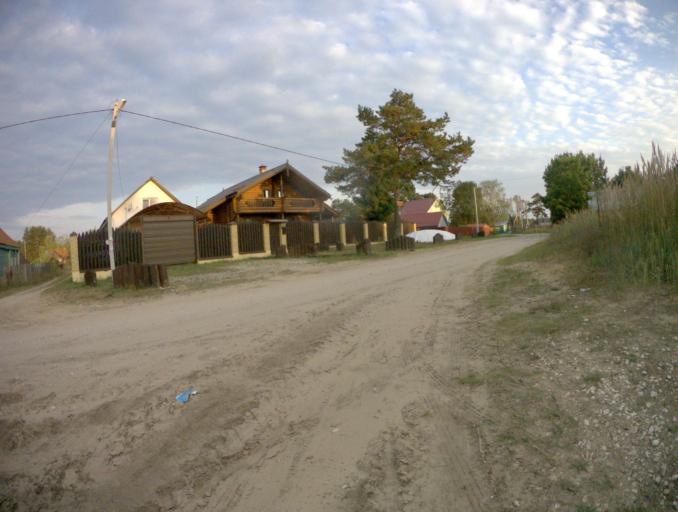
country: RU
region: Vladimir
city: Raduzhnyy
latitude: 56.0297
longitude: 40.3865
